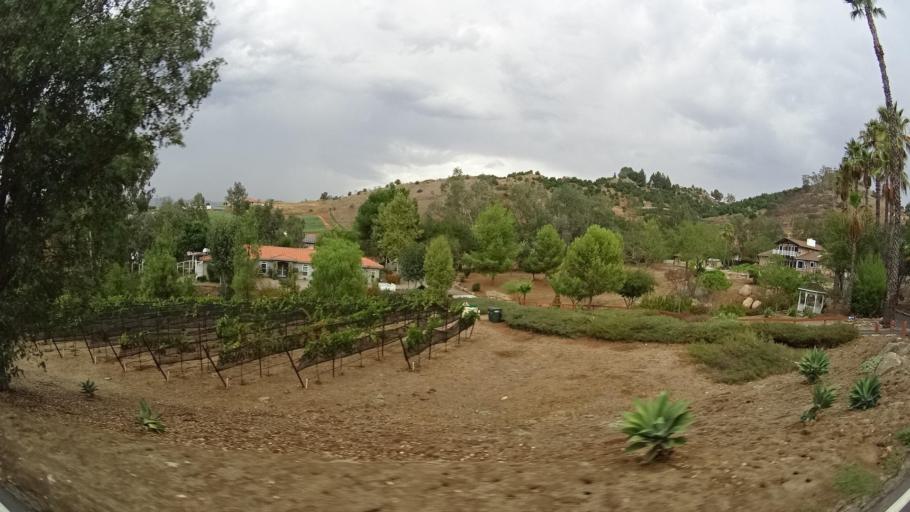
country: US
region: California
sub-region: San Diego County
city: San Pasqual
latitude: 33.0680
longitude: -116.9956
